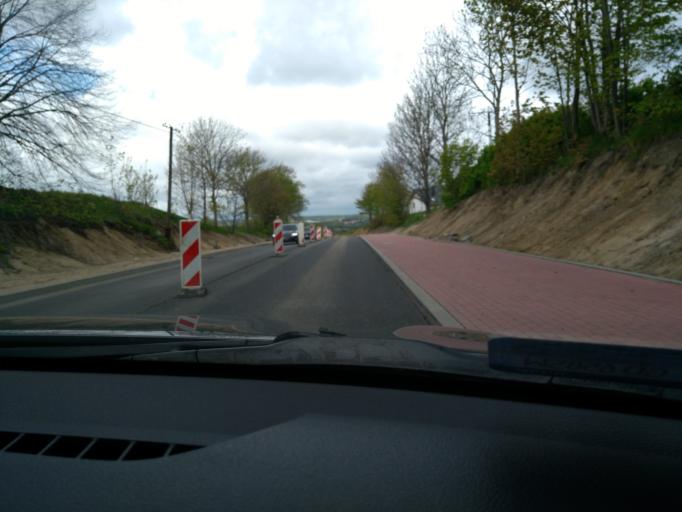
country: PL
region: Pomeranian Voivodeship
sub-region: Powiat kartuski
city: Kartuzy
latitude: 54.3455
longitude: 18.1547
